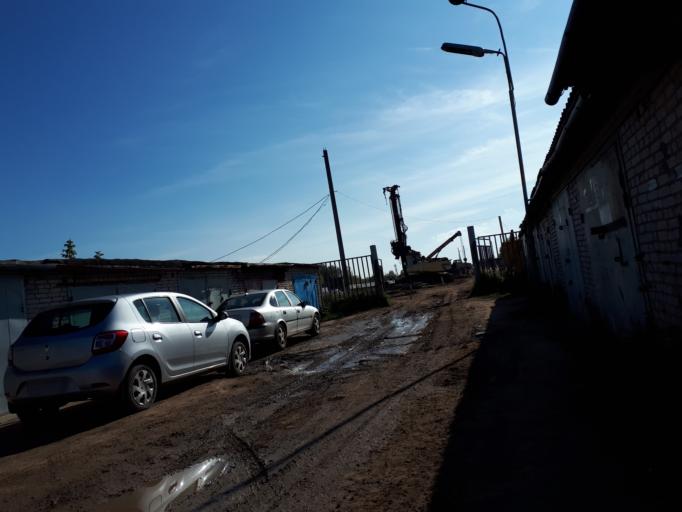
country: BY
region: Vitebsk
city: Vitebsk
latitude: 55.1682
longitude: 30.2456
